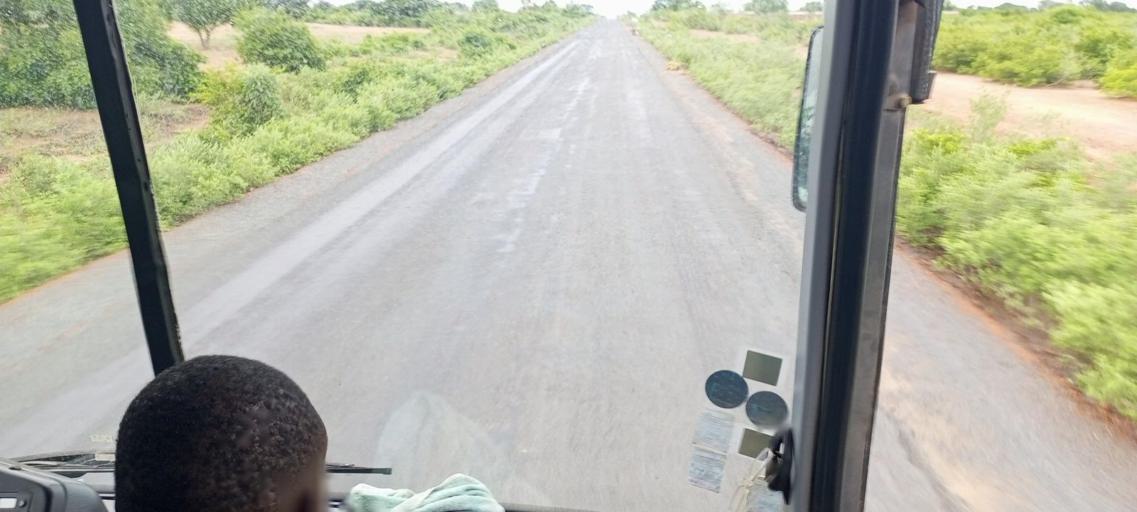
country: ML
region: Sikasso
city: Koutiala
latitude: 12.5721
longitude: -5.6031
